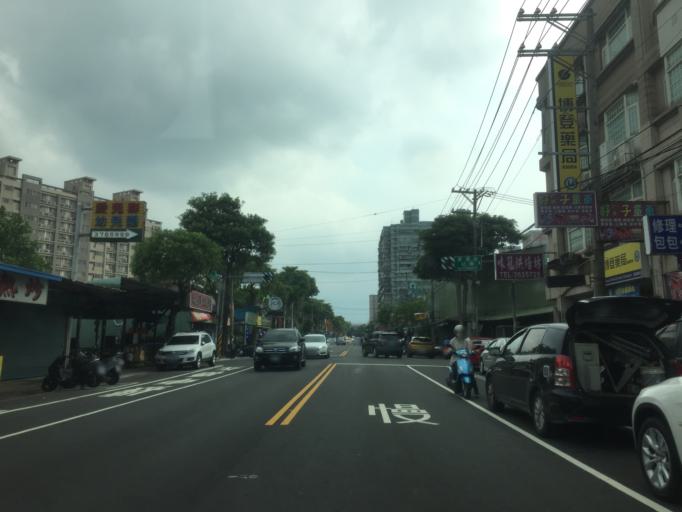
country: TW
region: Taiwan
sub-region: Taoyuan
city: Taoyuan
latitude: 24.9622
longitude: 121.3067
